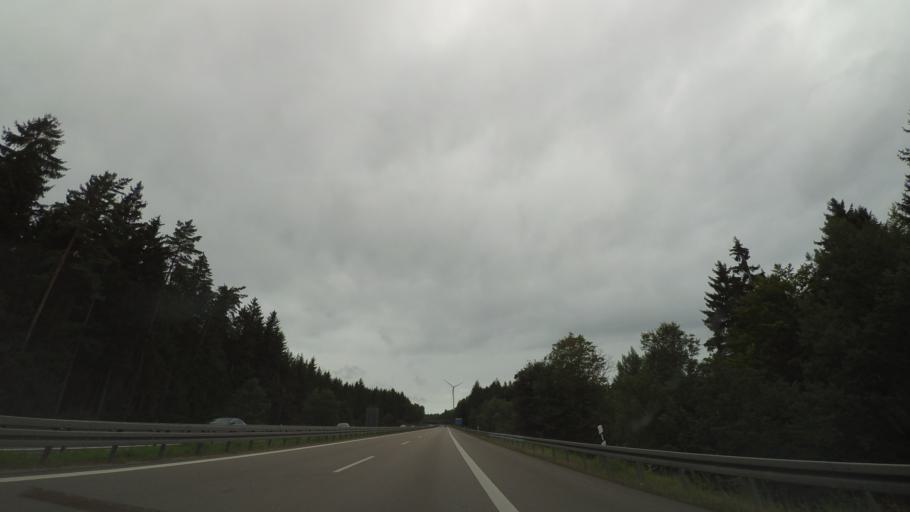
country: DE
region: Bavaria
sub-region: Regierungsbezirk Mittelfranken
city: Alfeld
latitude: 49.4095
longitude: 11.5332
